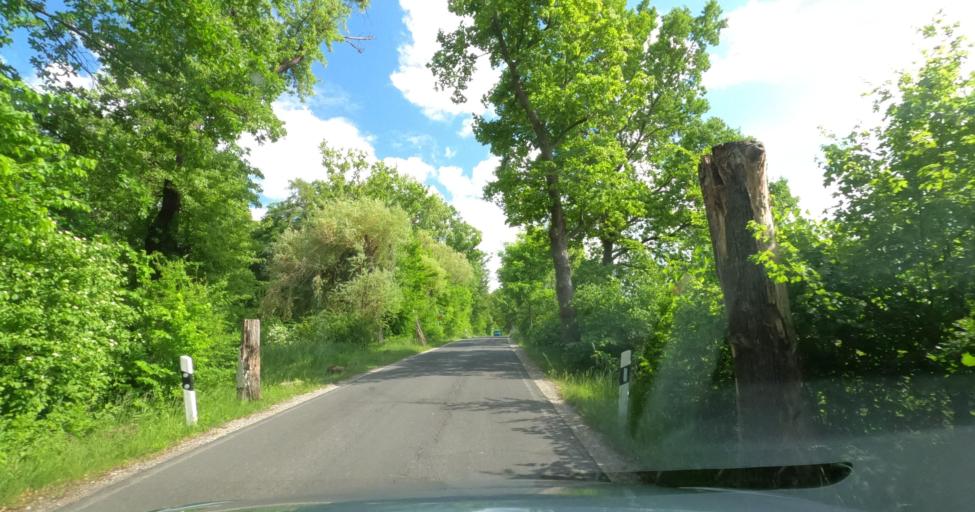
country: DE
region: Thuringia
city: Vollersroda
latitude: 50.9471
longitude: 11.3462
